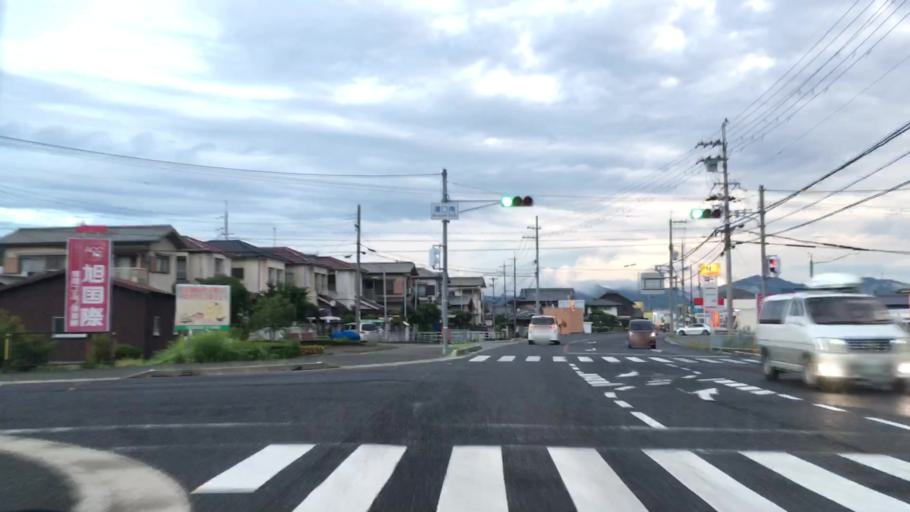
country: JP
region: Hyogo
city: Himeji
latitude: 34.9245
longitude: 134.7443
